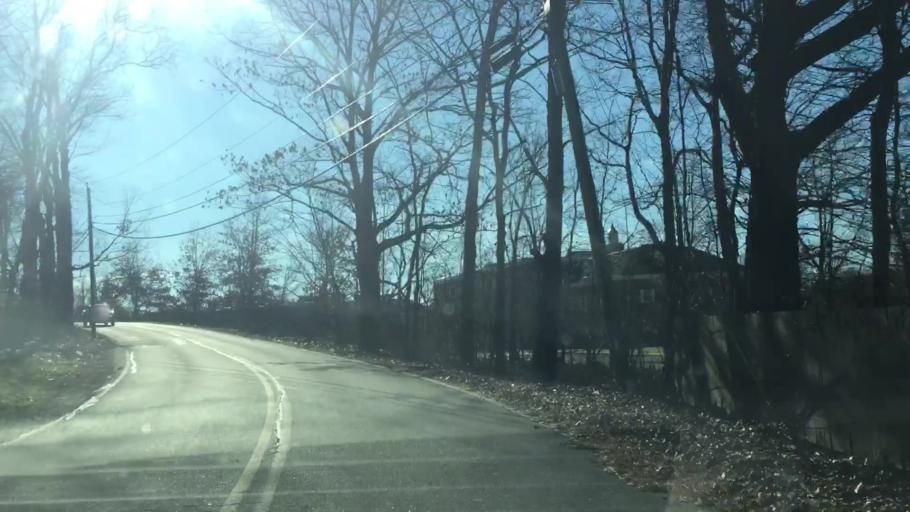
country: US
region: Massachusetts
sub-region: Essex County
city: Andover
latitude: 42.6627
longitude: -71.1073
